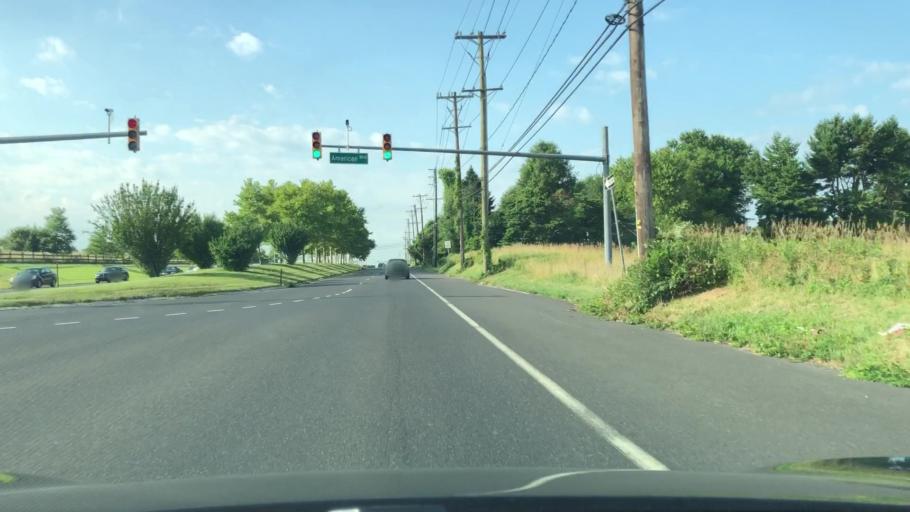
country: US
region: New Jersey
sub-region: Mercer County
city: Ewing
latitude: 40.2981
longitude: -74.8115
